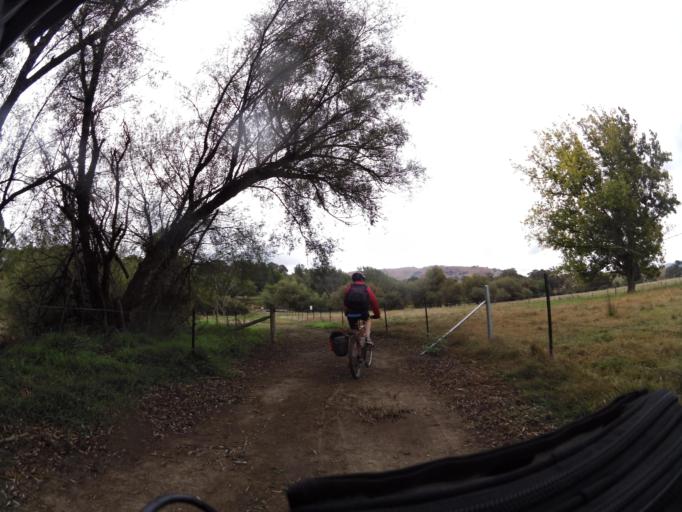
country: AU
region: New South Wales
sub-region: Albury Municipality
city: East Albury
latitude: -36.1935
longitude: 147.3109
